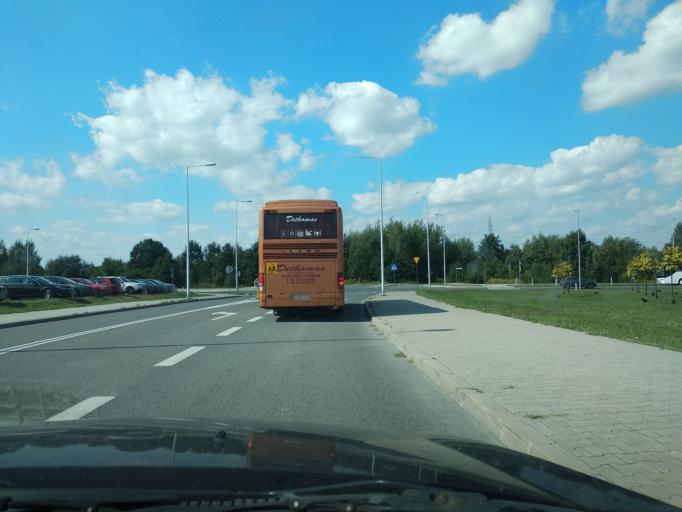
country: PL
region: Swietokrzyskie
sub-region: Powiat kielecki
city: Kostomloty Pierwsze
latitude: 50.9005
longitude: 20.5823
